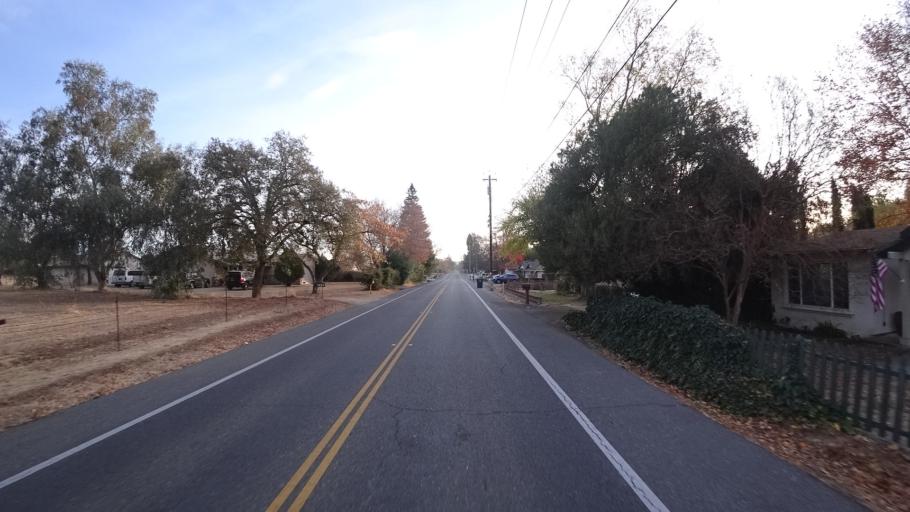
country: US
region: California
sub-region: Sacramento County
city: Citrus Heights
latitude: 38.7185
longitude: -121.2834
